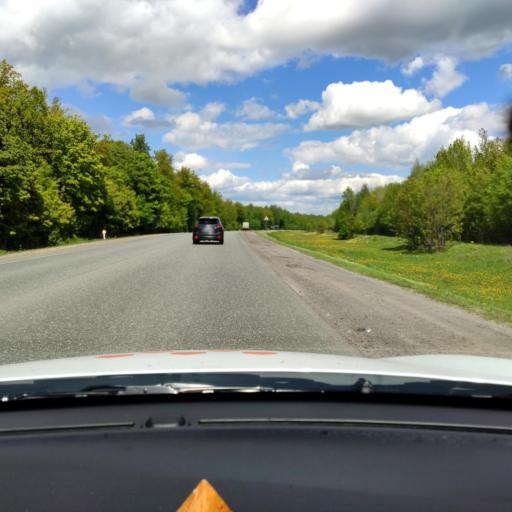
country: RU
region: Tatarstan
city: Verkhniy Uslon
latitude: 55.6852
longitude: 48.8714
